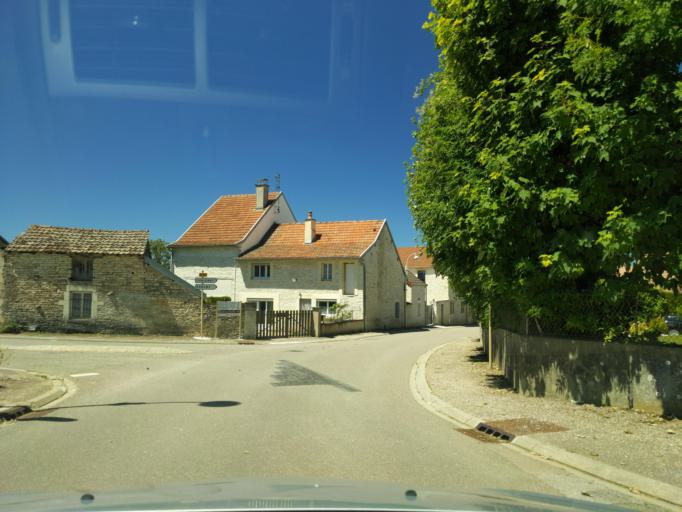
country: FR
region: Bourgogne
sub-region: Departement de la Cote-d'Or
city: Saint-Julien
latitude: 47.4384
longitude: 5.0968
